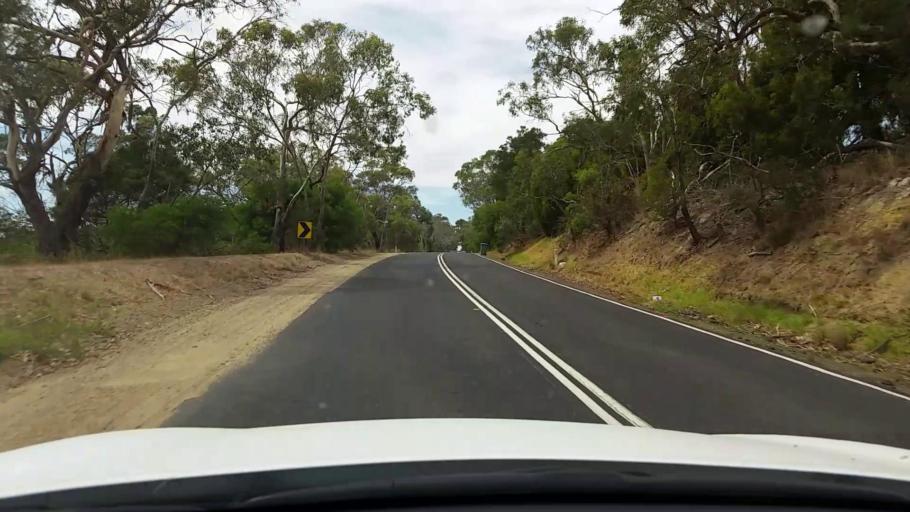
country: AU
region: Victoria
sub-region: Mornington Peninsula
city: Mount Martha
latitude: -38.2959
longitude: 145.0462
